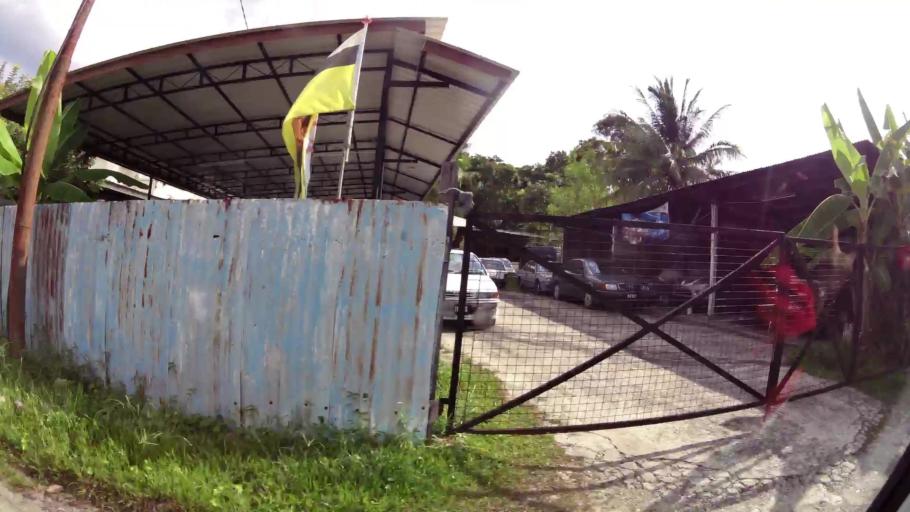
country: BN
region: Brunei and Muara
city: Bandar Seri Begawan
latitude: 4.9563
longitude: 114.9717
